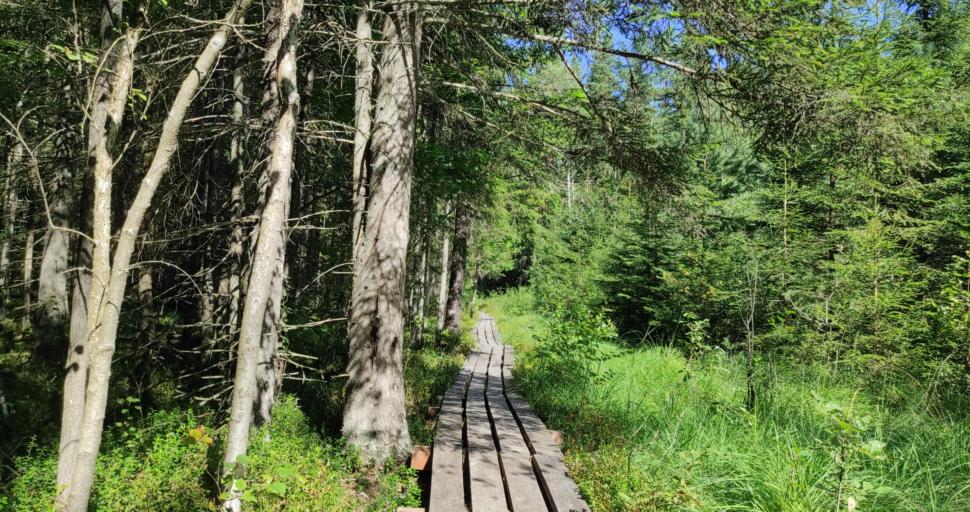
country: LT
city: Skuodas
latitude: 56.2430
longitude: 21.3983
